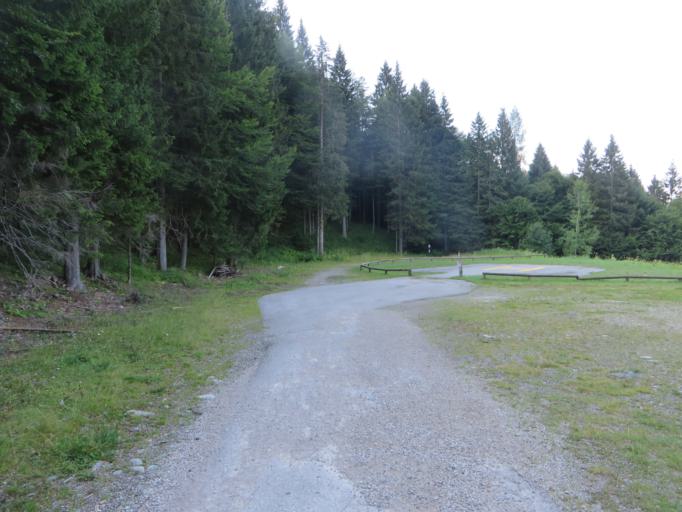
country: IT
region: Trentino-Alto Adige
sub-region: Provincia di Trento
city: Carisolo
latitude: 46.2185
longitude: 10.8275
